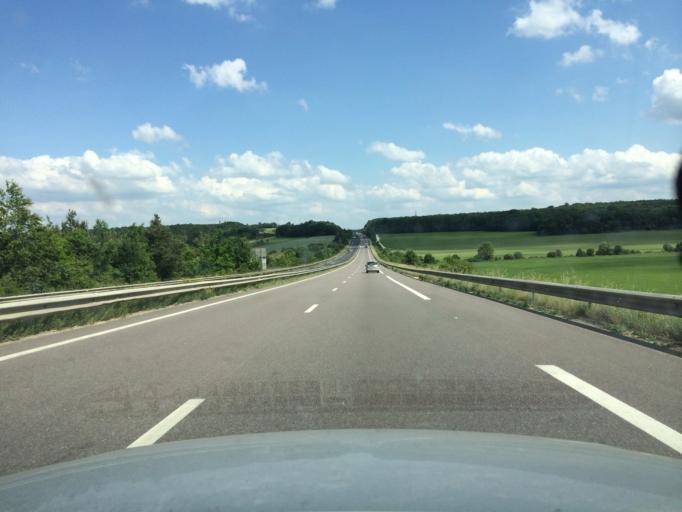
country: FR
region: Lorraine
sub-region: Departement de Meurthe-et-Moselle
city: Foug
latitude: 48.6793
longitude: 5.7513
